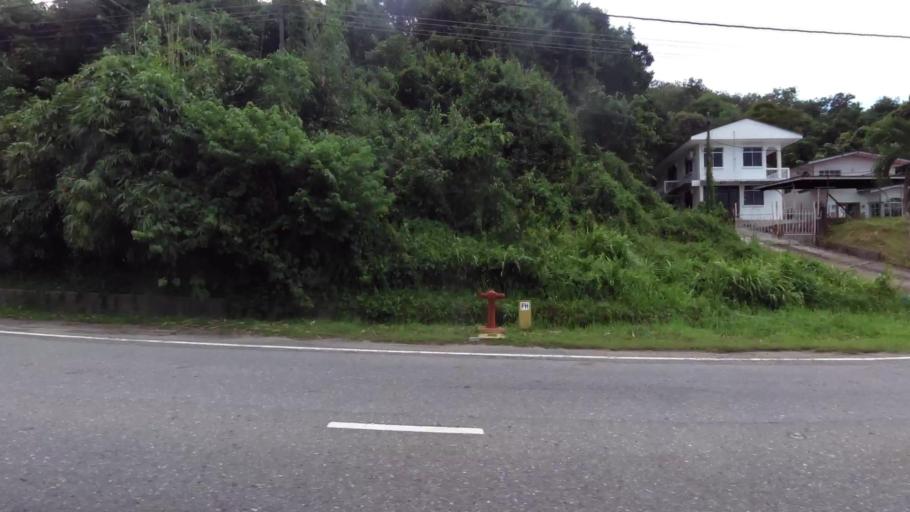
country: BN
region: Brunei and Muara
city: Bandar Seri Begawan
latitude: 4.9034
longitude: 114.9919
